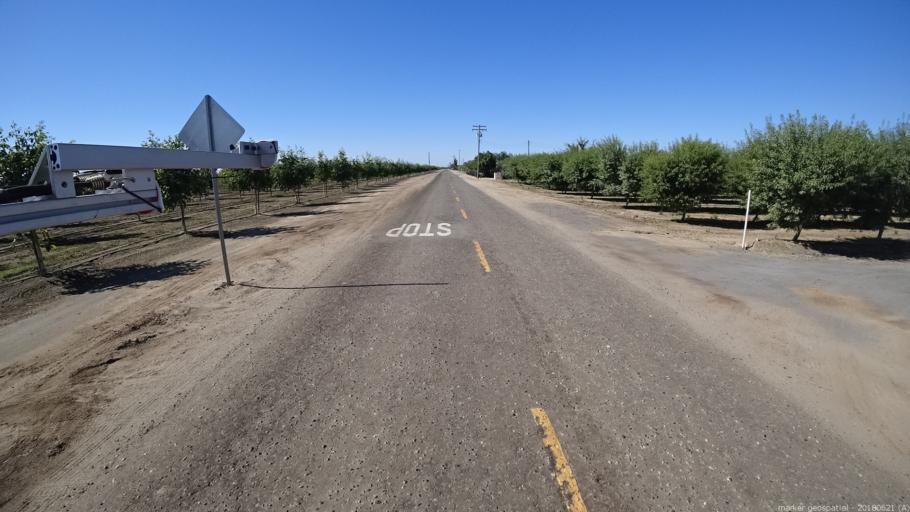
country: US
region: California
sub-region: Fresno County
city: Biola
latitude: 36.8497
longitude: -120.0464
